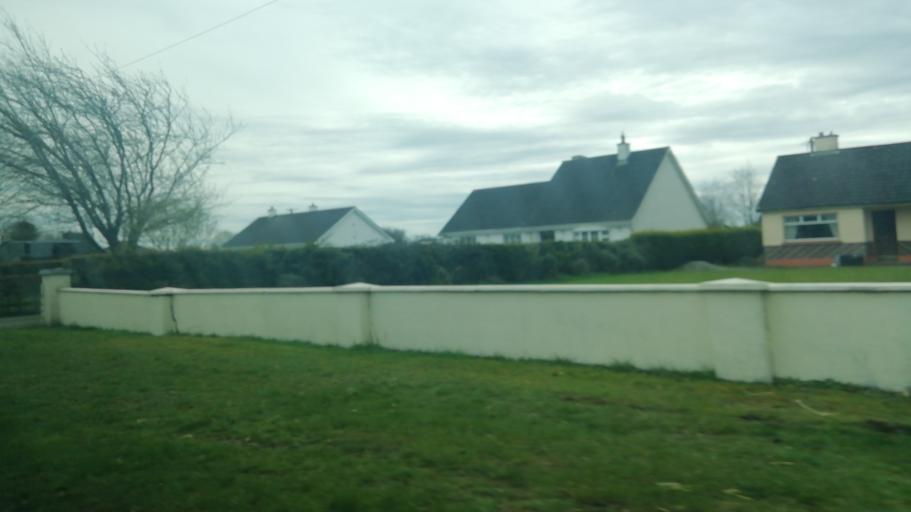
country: IE
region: Leinster
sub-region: Kildare
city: Derrinturn
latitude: 53.3472
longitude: -6.9535
